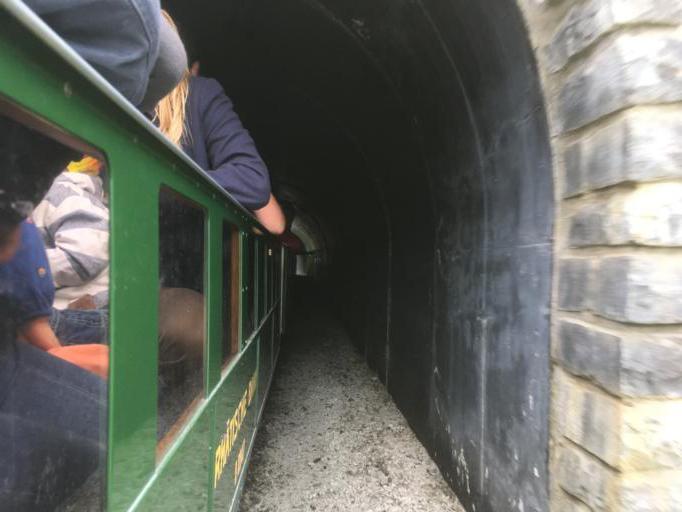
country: CH
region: Valais
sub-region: Monthey District
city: Port-Valais
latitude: 46.3850
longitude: 6.8563
